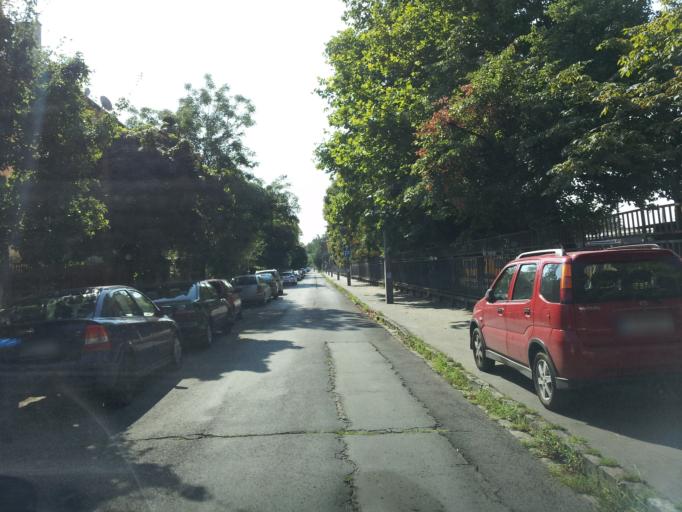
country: HU
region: Budapest
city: Budapest XIV. keruelet
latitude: 47.5192
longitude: 19.0933
